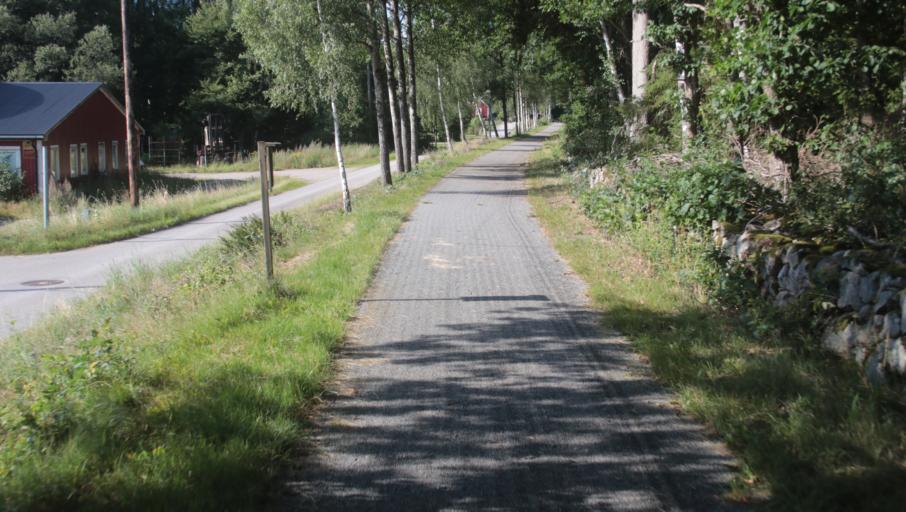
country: SE
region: Blekinge
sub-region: Karlshamns Kommun
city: Svangsta
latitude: 56.3869
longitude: 14.6759
